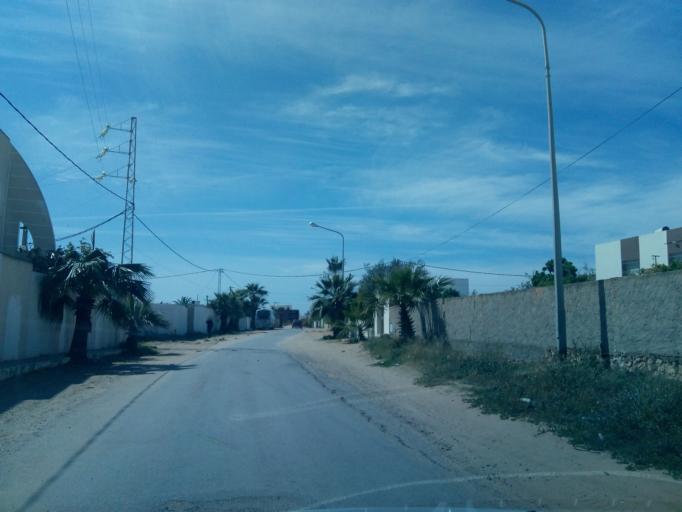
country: TN
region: Safaqis
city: Sfax
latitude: 34.7696
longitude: 10.6989
